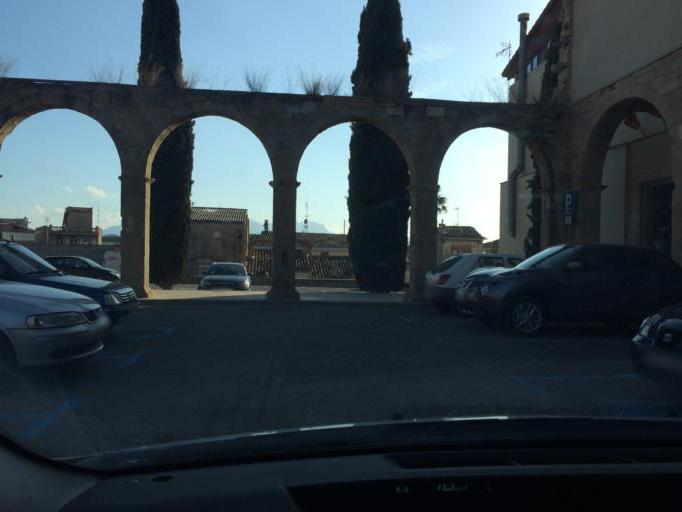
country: ES
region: Catalonia
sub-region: Provincia de Barcelona
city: Manresa
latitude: 41.7246
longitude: 1.8262
